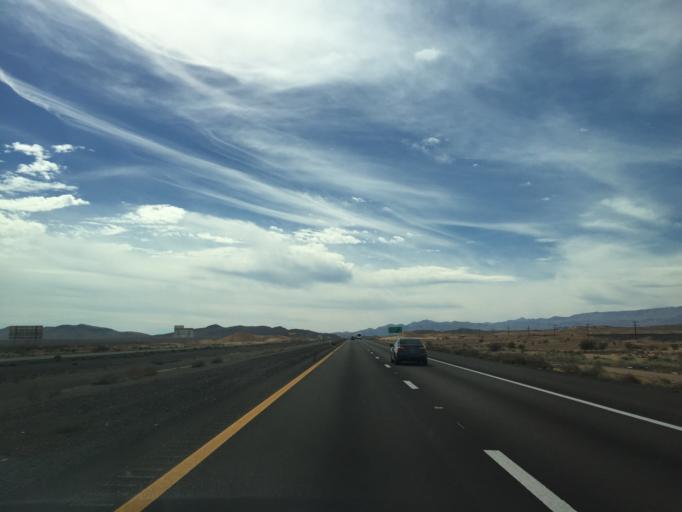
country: US
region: Nevada
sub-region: Clark County
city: Moapa Town
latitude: 36.4970
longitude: -114.7722
